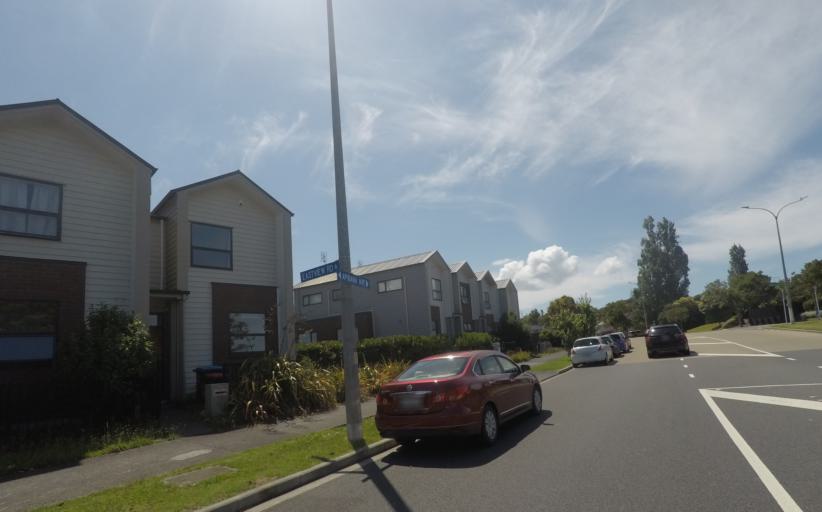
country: NZ
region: Auckland
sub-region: Auckland
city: Tamaki
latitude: -36.8725
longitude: 174.8529
